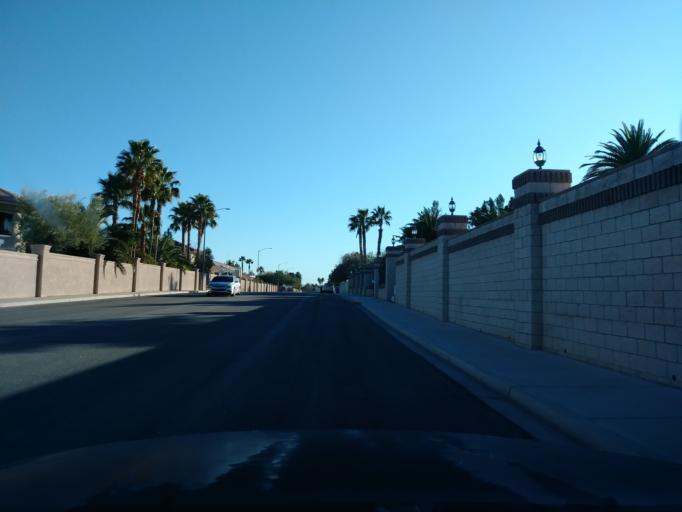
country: US
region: Nevada
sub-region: Clark County
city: Spring Valley
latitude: 36.1493
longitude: -115.2682
